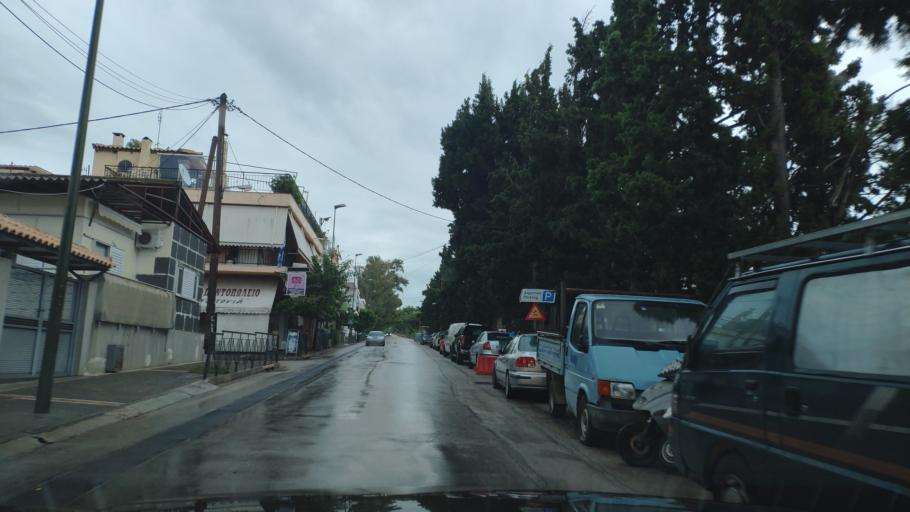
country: GR
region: Peloponnese
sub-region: Nomos Korinthias
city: Loutraki
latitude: 37.9674
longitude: 22.9812
